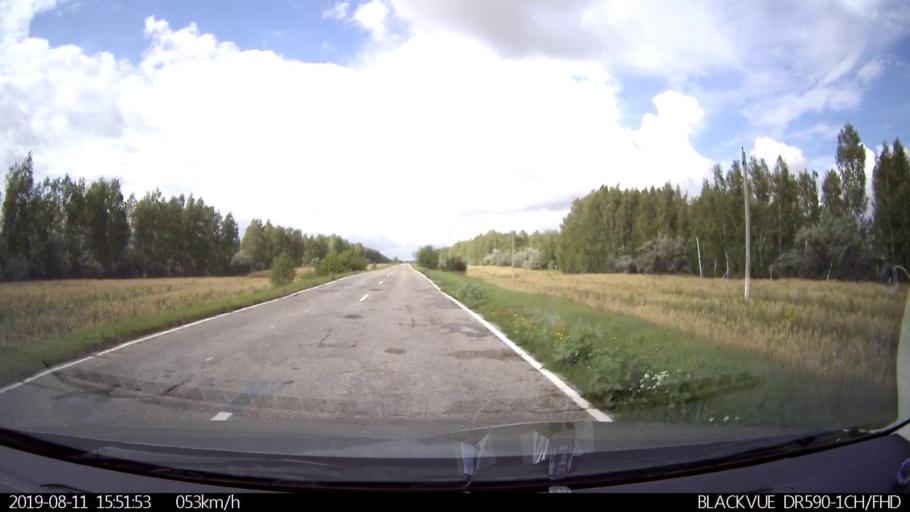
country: RU
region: Ulyanovsk
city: Ignatovka
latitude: 53.9223
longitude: 47.6562
